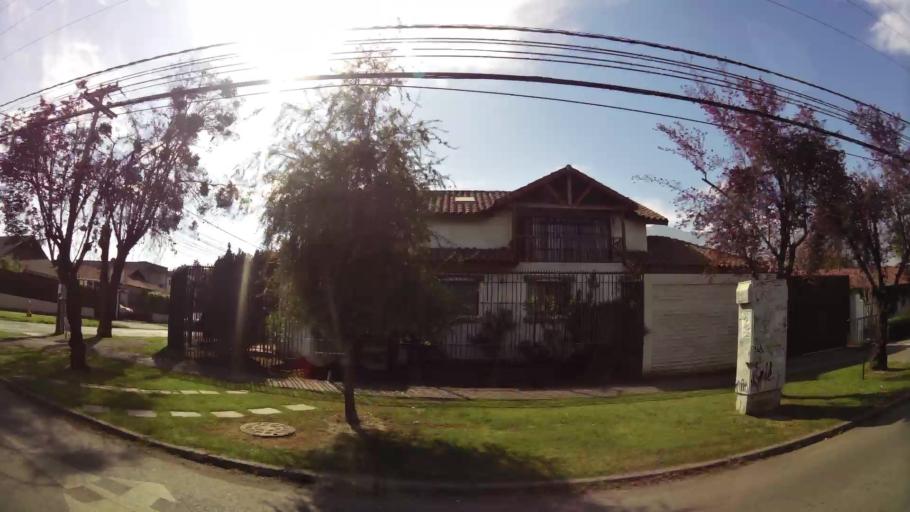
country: CL
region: Santiago Metropolitan
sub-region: Provincia de Santiago
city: Villa Presidente Frei, Nunoa, Santiago, Chile
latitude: -33.4530
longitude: -70.5552
